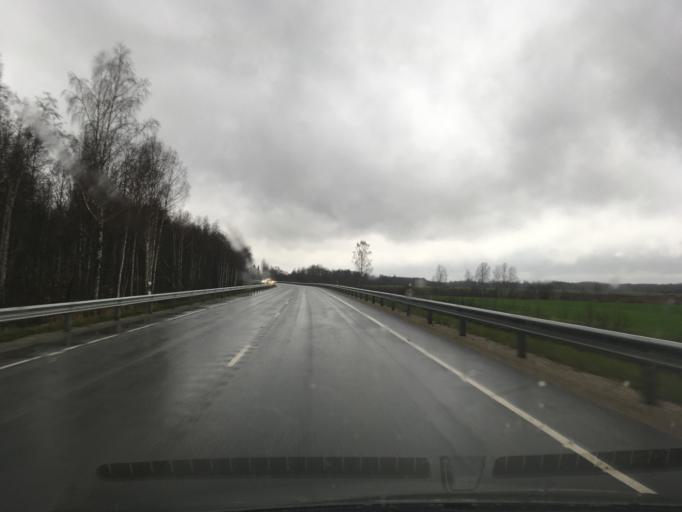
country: EE
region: Laeaene
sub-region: Lihula vald
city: Lihula
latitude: 58.7792
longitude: 23.9954
